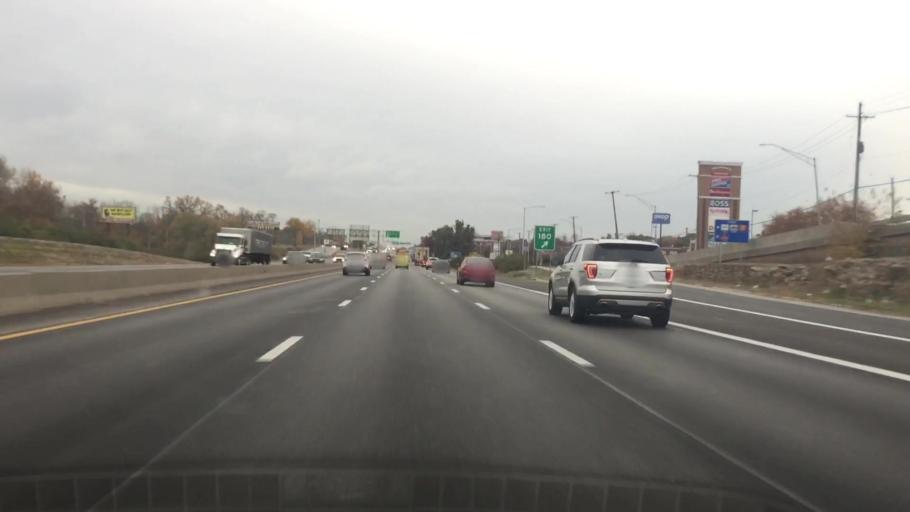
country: US
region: Missouri
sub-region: Jackson County
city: Grandview
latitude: 38.9061
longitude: -94.5241
